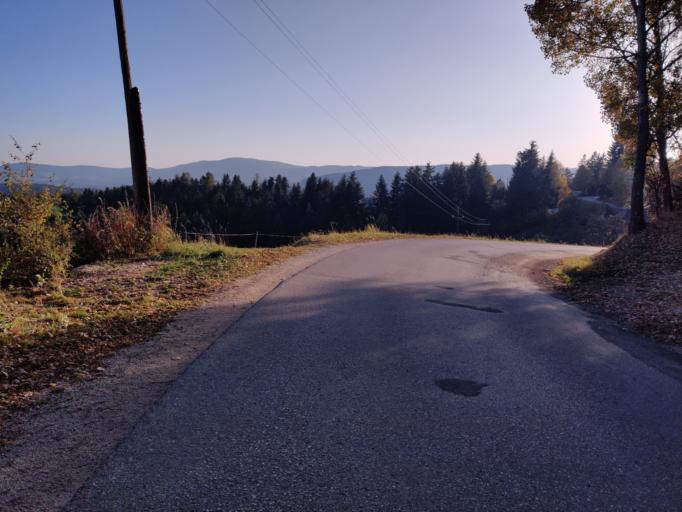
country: AT
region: Styria
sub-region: Politischer Bezirk Hartberg-Fuerstenfeld
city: Sankt Jakob im Walde
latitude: 47.4729
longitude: 15.7910
